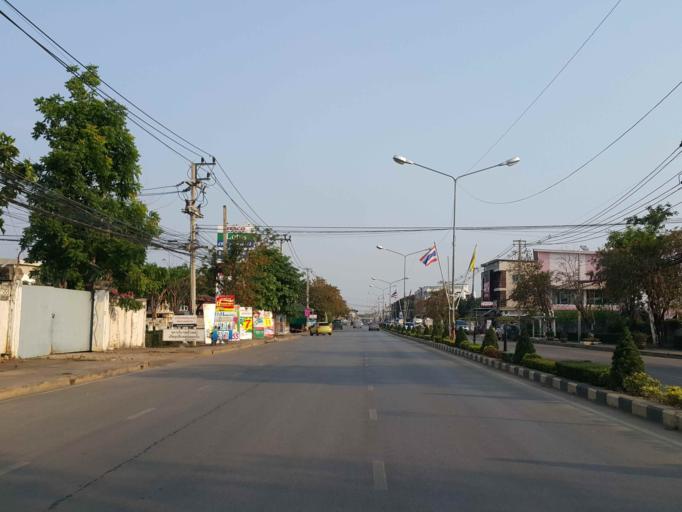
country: TH
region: Sukhothai
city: Sawankhalok
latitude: 17.3062
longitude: 99.8326
